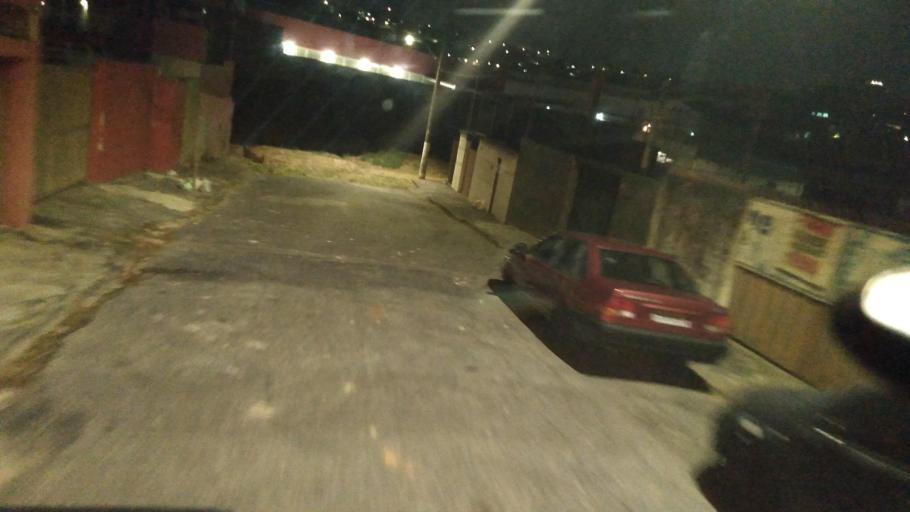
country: BR
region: Minas Gerais
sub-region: Belo Horizonte
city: Belo Horizonte
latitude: -19.8930
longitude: -43.9623
